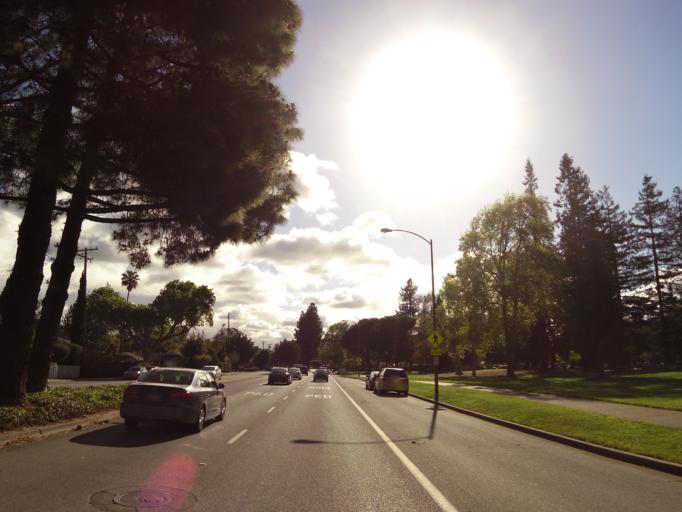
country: US
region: California
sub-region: Santa Clara County
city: Mountain View
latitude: 37.3735
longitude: -122.0813
